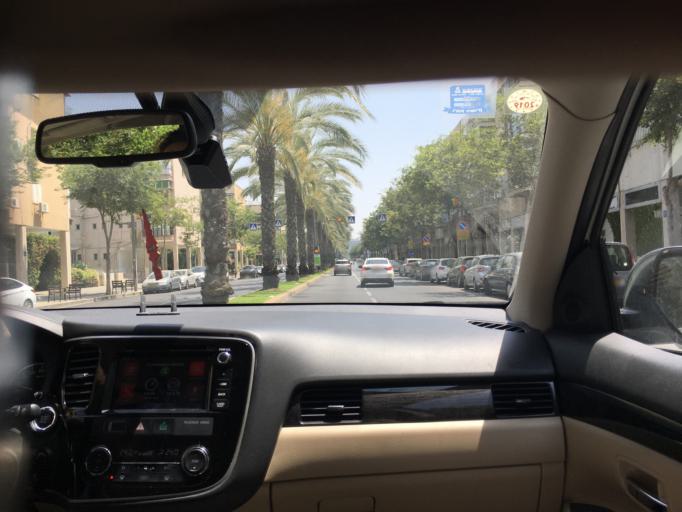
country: IL
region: Tel Aviv
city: Tel Aviv
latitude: 32.0933
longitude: 34.7833
